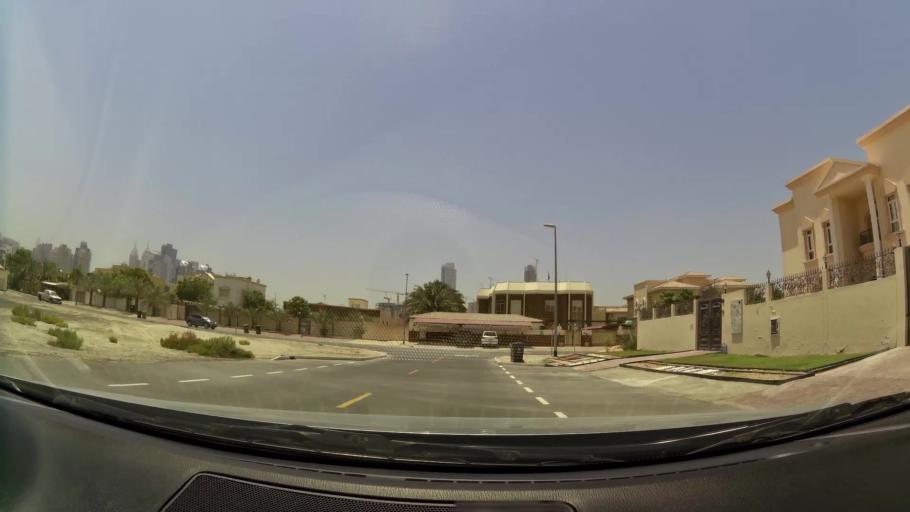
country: AE
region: Dubai
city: Dubai
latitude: 25.1018
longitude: 55.1880
